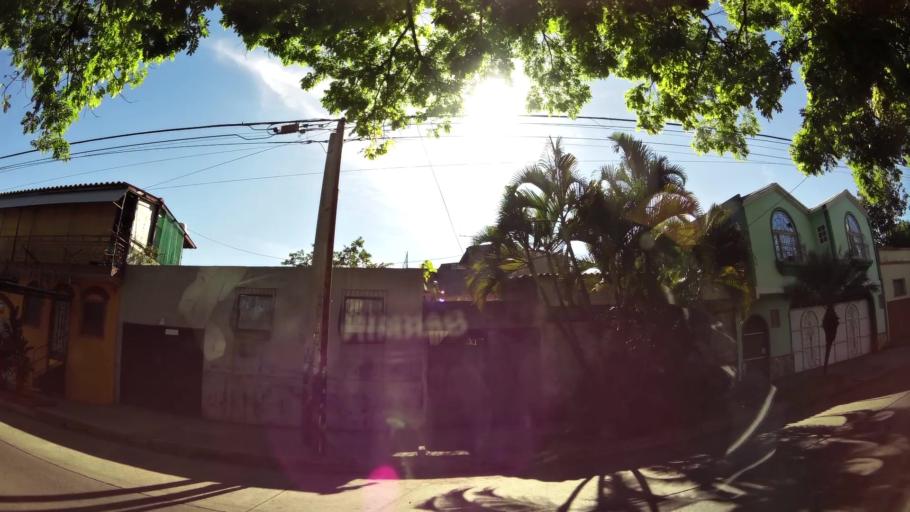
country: SV
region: Santa Ana
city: Santa Ana
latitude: 13.9798
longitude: -89.5679
